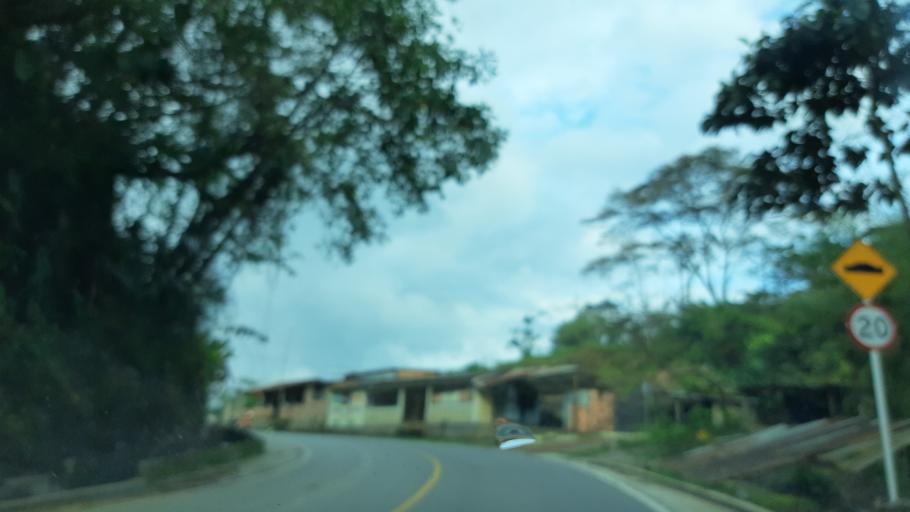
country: CO
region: Boyaca
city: Santa Maria
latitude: 4.8611
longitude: -73.2543
